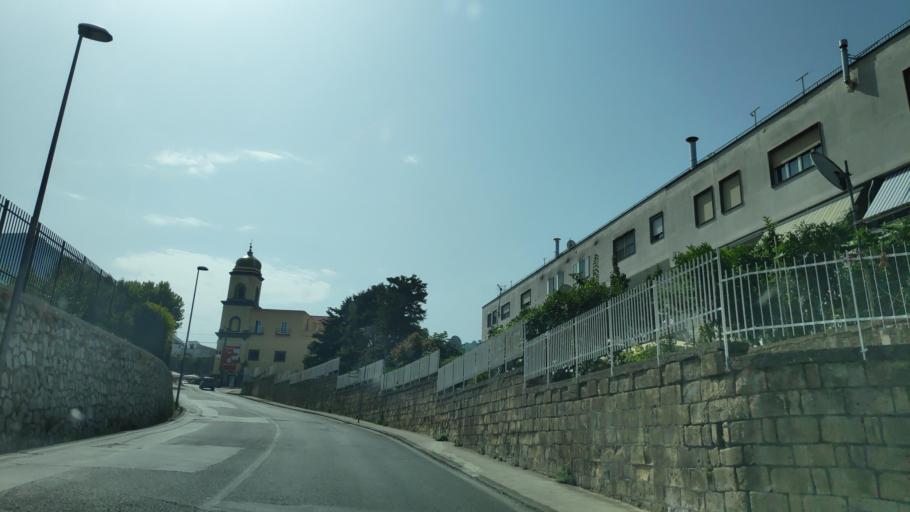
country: IT
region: Campania
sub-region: Provincia di Napoli
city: Piano di Sorrento
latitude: 40.6294
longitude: 14.4101
